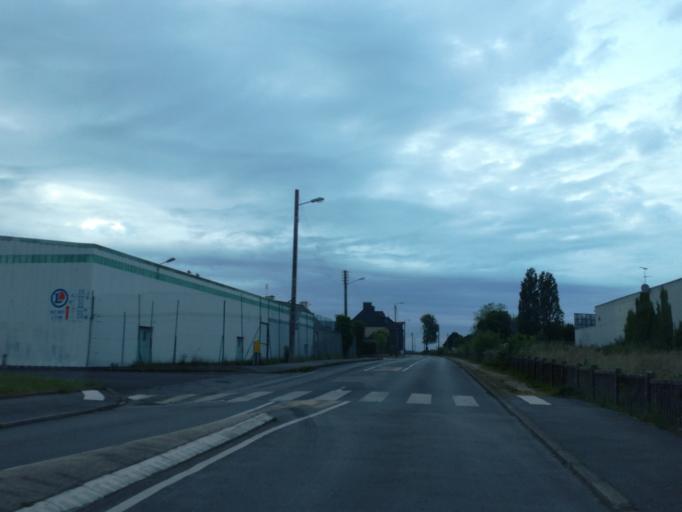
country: FR
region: Brittany
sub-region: Departement des Cotes-d'Armor
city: Loudeac
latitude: 48.1759
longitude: -2.7605
